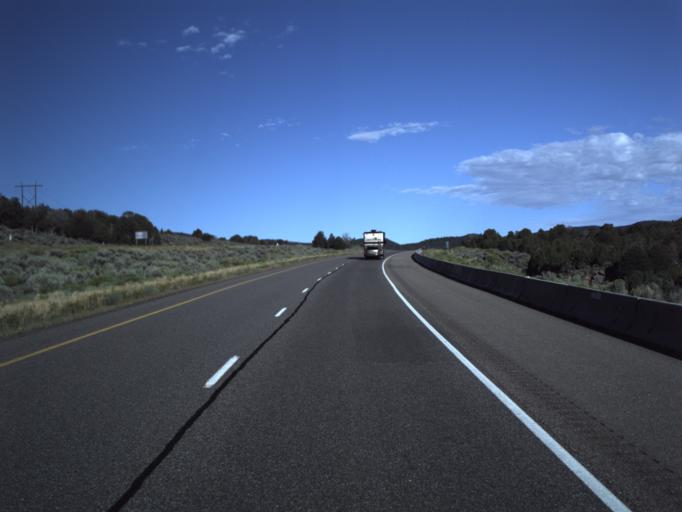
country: US
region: Utah
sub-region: Sevier County
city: Monroe
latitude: 38.5651
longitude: -112.4380
